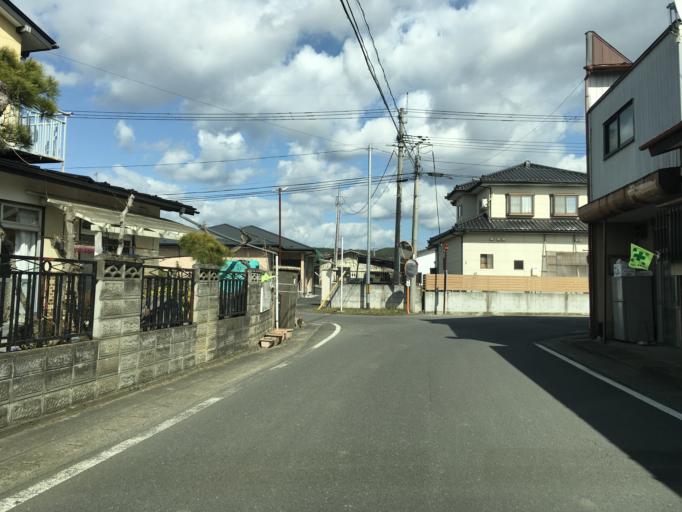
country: JP
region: Iwate
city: Ichinoseki
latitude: 38.7427
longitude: 141.2659
